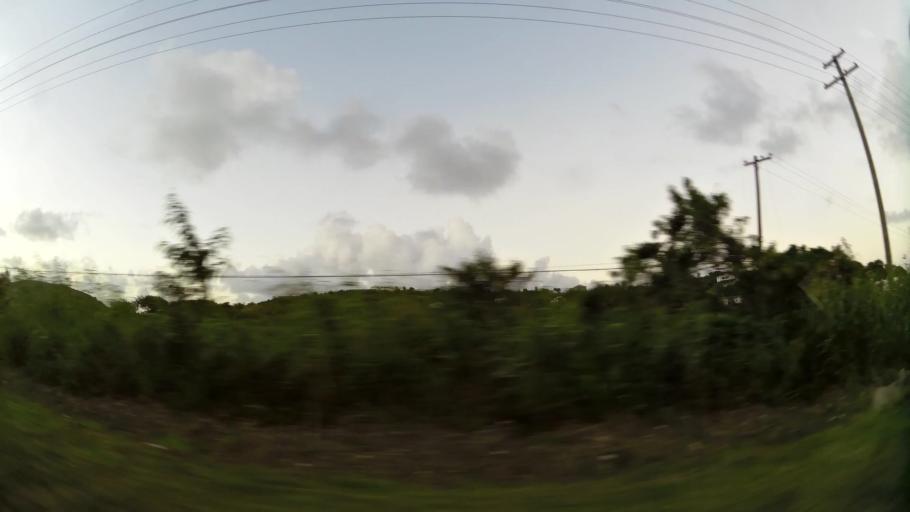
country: AG
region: Saint George
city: Piggotts
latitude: 17.1304
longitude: -61.8068
